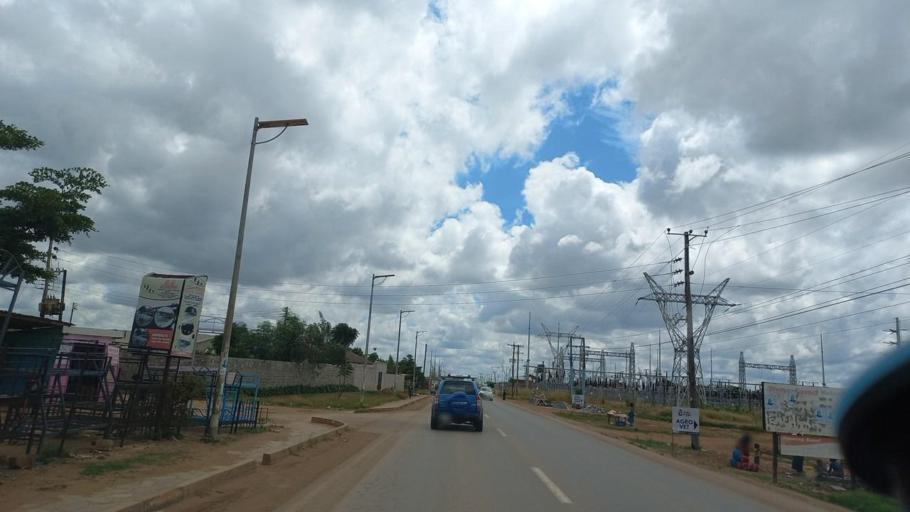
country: ZM
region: Lusaka
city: Lusaka
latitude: -15.4524
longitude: 28.3193
